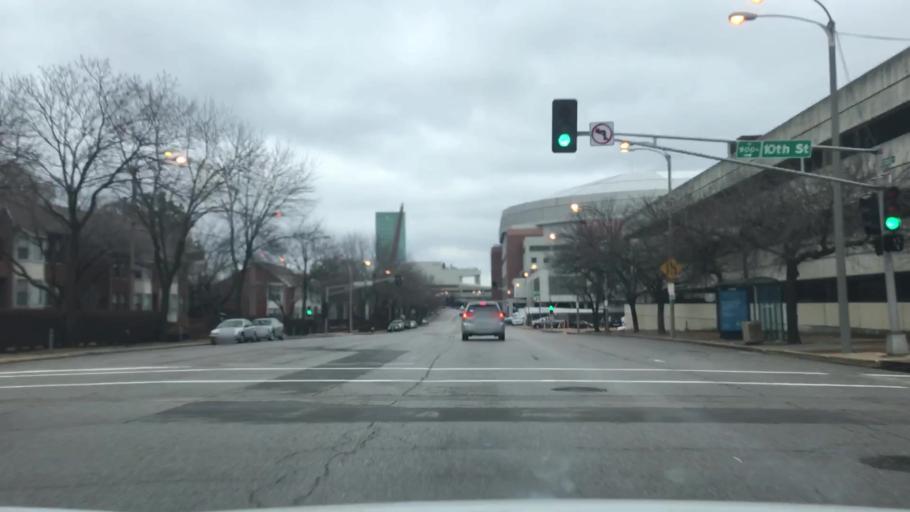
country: US
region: Missouri
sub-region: City of Saint Louis
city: St. Louis
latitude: 38.6348
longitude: -90.1925
